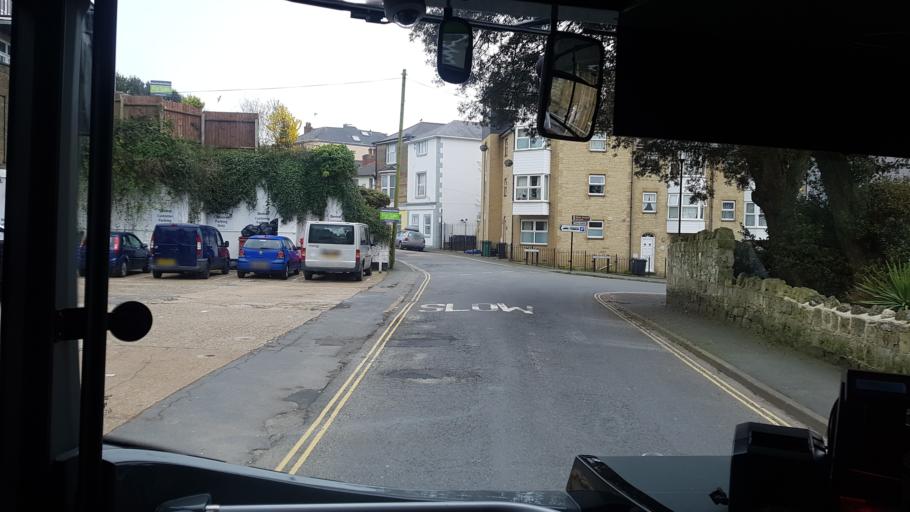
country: GB
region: England
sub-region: Isle of Wight
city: Ventnor
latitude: 50.5954
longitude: -1.2016
